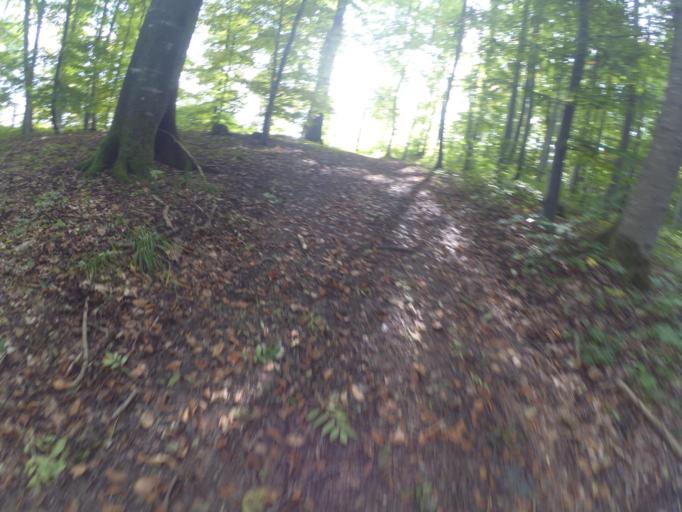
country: DE
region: Baden-Wuerttemberg
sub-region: Regierungsbezirk Stuttgart
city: Heubach
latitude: 48.7806
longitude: 9.9183
